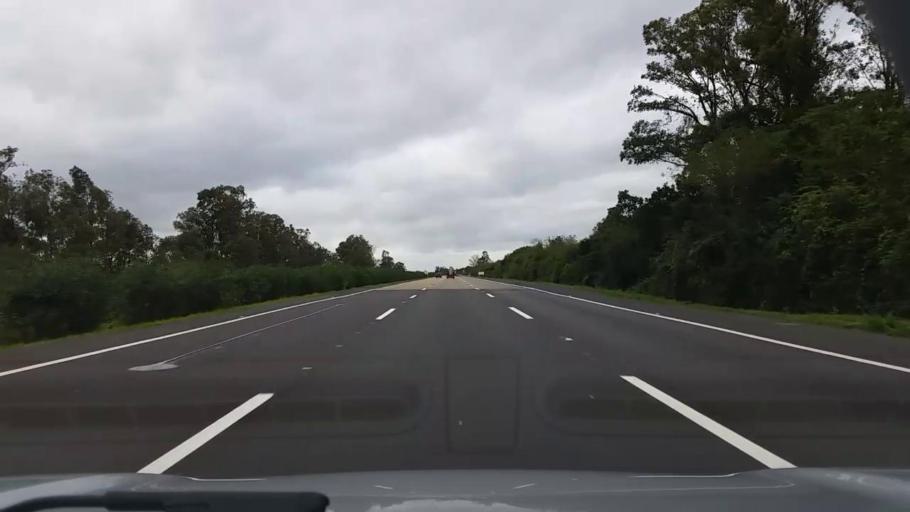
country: BR
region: Rio Grande do Sul
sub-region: Rolante
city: Rolante
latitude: -29.8851
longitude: -50.5783
